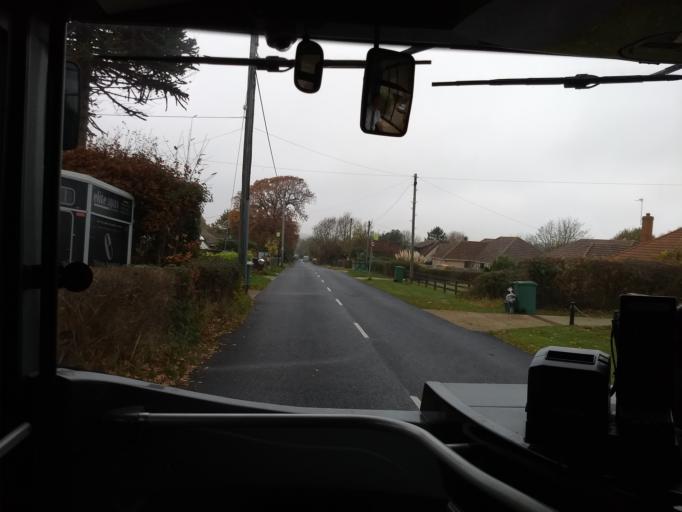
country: GB
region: England
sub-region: Isle of Wight
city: Newchurch
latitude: 50.6540
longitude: -1.2069
